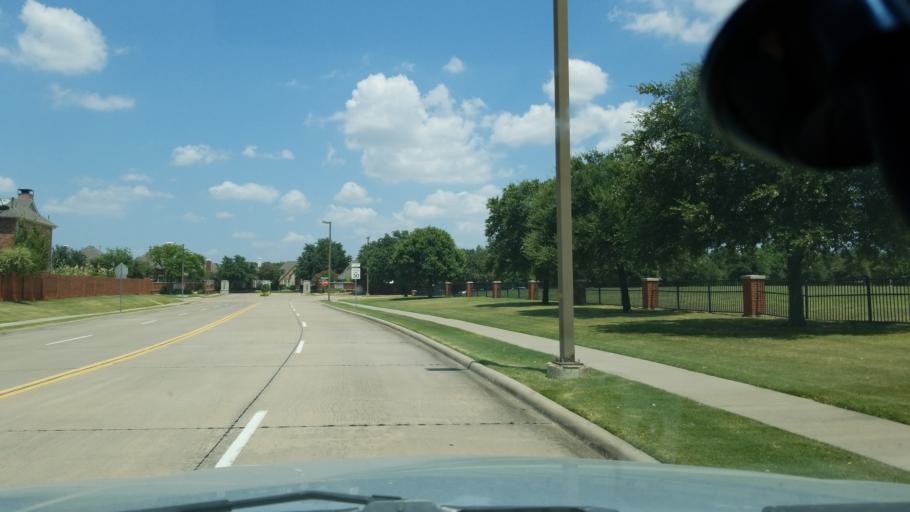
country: US
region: Texas
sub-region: Dallas County
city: Farmers Branch
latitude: 32.9206
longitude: -96.9493
